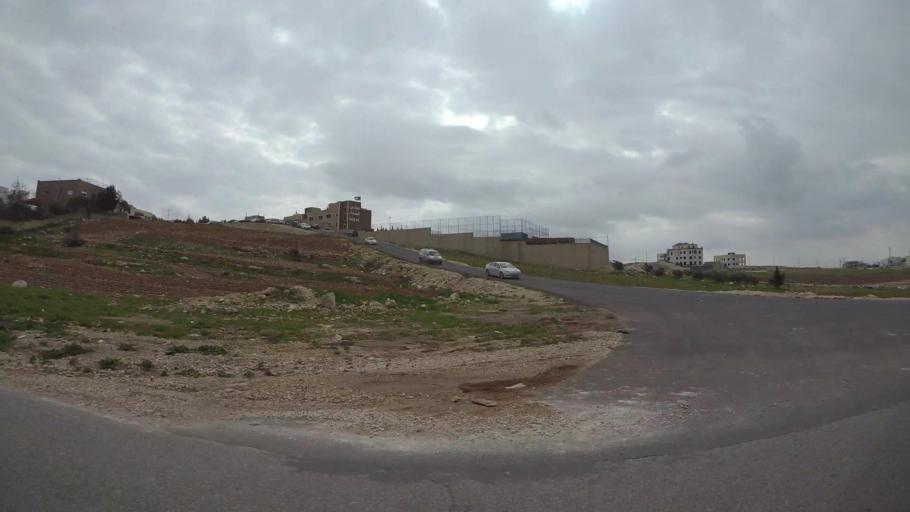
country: JO
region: Amman
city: Wadi as Sir
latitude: 31.9315
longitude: 35.8496
